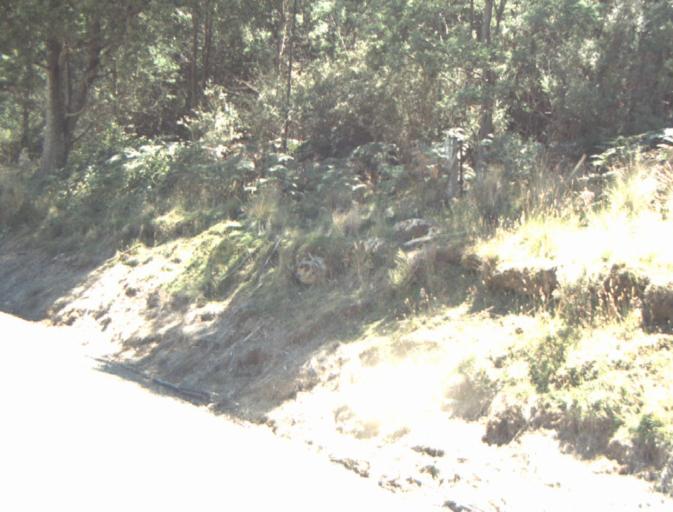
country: AU
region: Tasmania
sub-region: Dorset
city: Scottsdale
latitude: -41.3223
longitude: 147.4519
